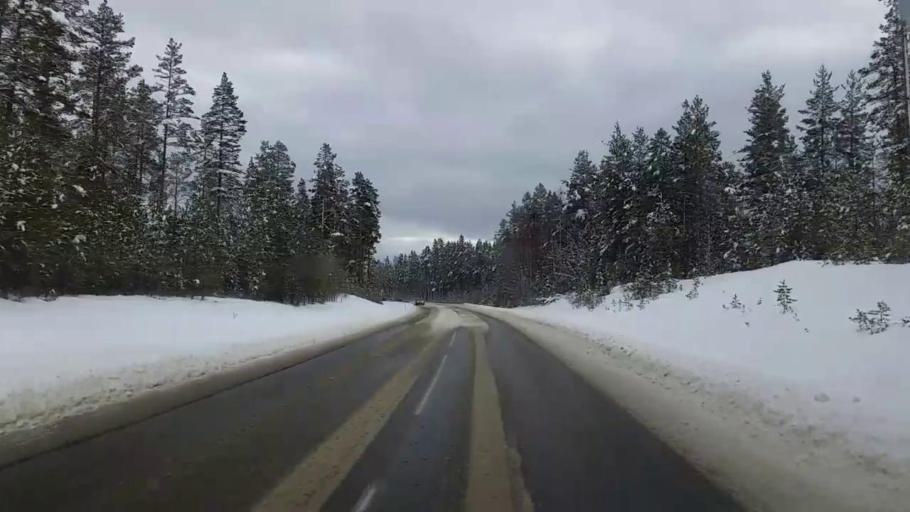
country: SE
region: Vaesternorrland
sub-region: Ange Kommun
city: Ange
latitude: 62.0606
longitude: 15.1153
